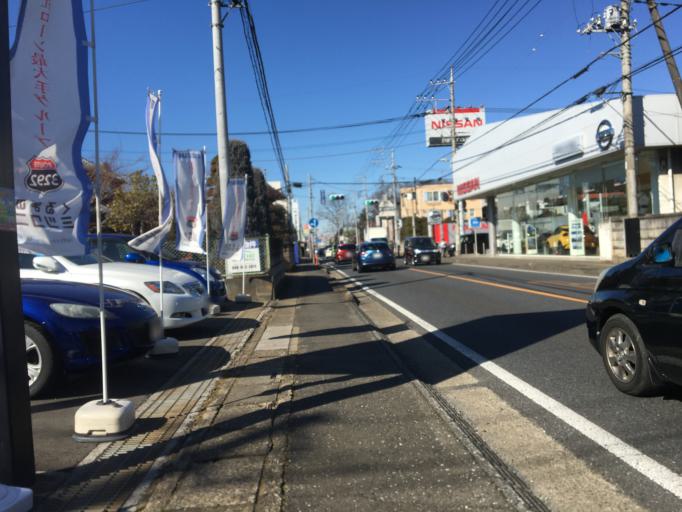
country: JP
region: Saitama
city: Oi
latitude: 35.8329
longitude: 139.5309
